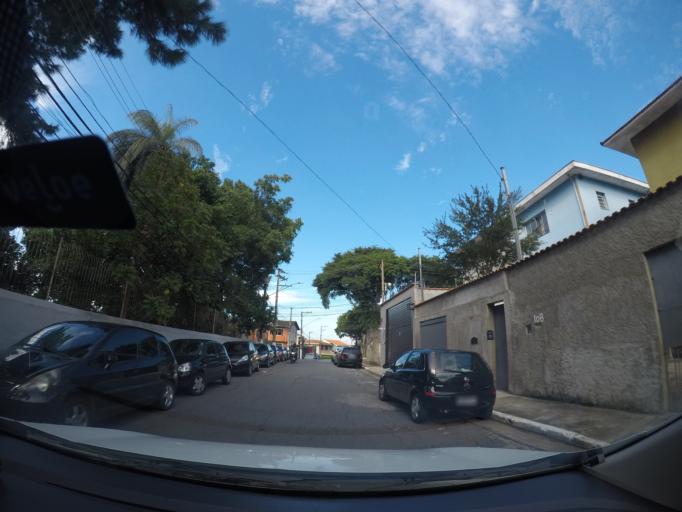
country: BR
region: Sao Paulo
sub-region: Diadema
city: Diadema
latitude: -23.6338
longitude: -46.6454
